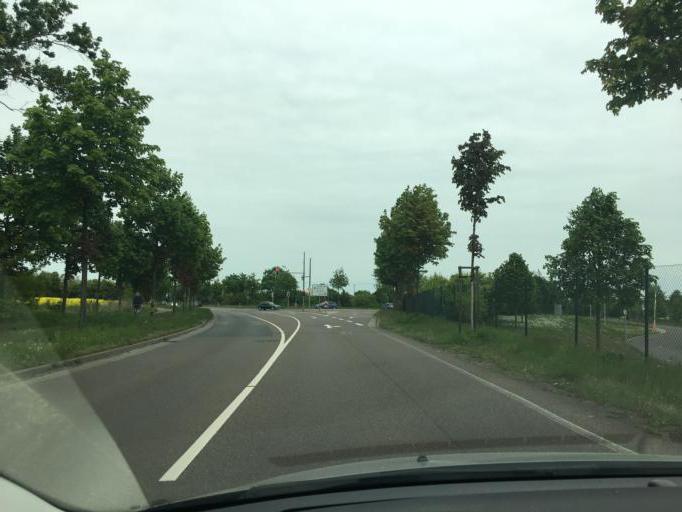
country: DE
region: Saxony
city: Taucha
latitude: 51.3957
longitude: 12.4356
